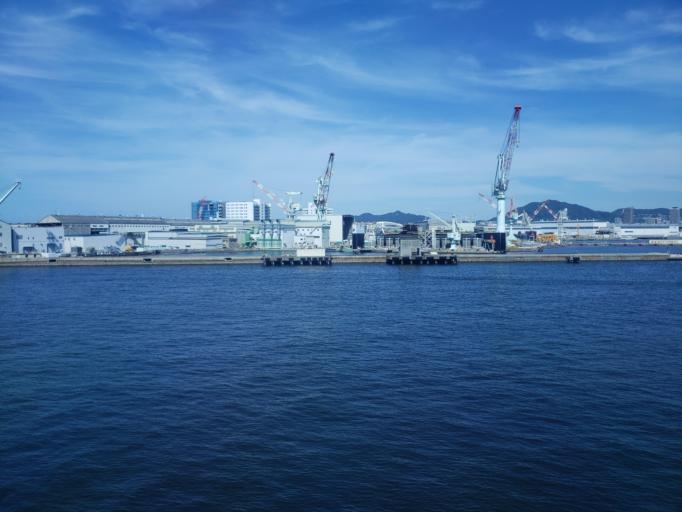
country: JP
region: Hyogo
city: Kobe
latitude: 34.6545
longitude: 135.1886
